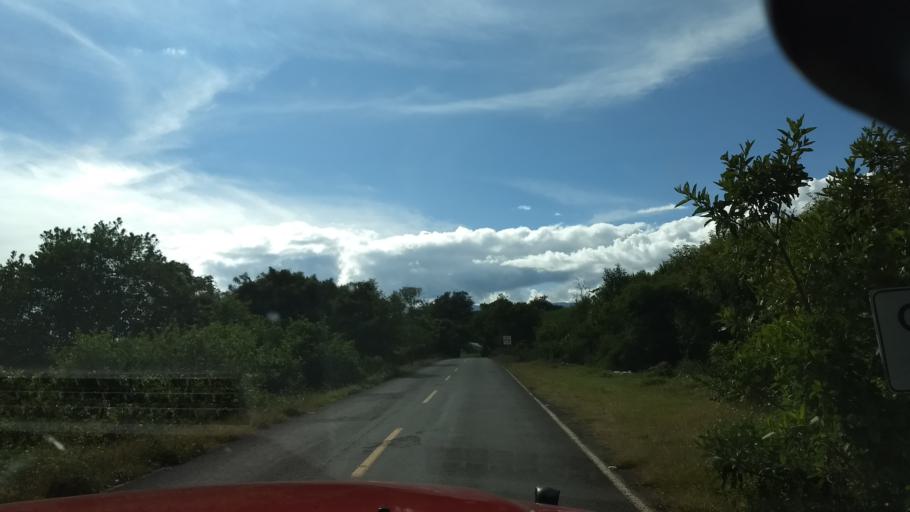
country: MX
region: Colima
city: Suchitlan
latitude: 19.4680
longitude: -103.7555
